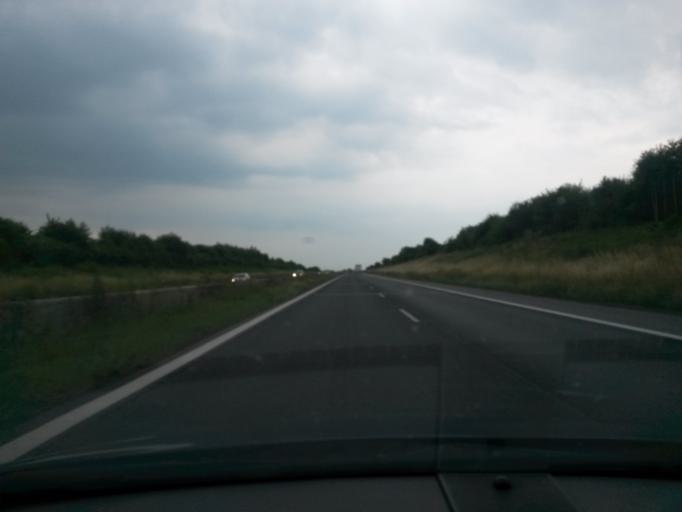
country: PL
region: Silesian Voivodeship
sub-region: Powiat czestochowski
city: Borowno
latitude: 50.9651
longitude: 19.2588
